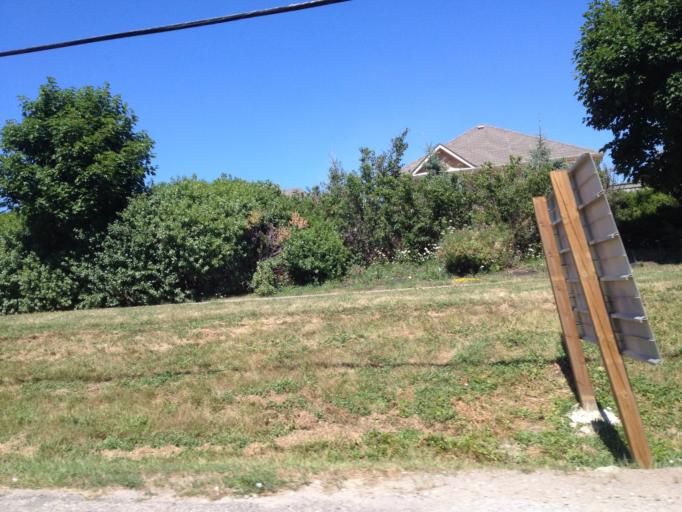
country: CA
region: Ontario
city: Brampton
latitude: 43.7316
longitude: -79.8219
